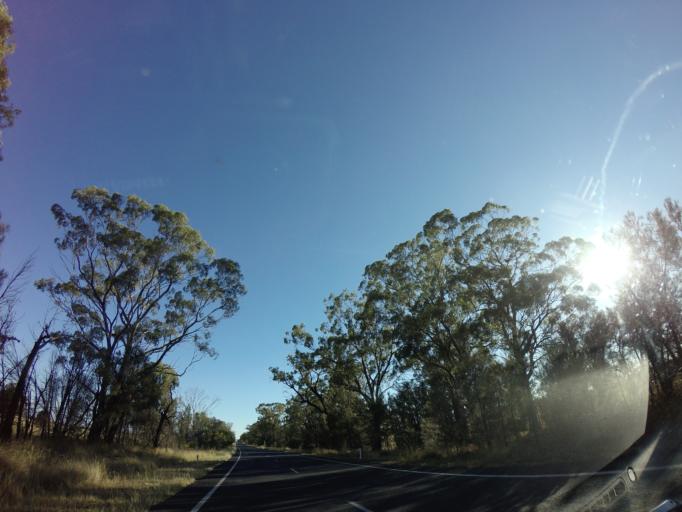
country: AU
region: New South Wales
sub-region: Gilgandra
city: Gilgandra
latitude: -31.5868
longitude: 148.7735
